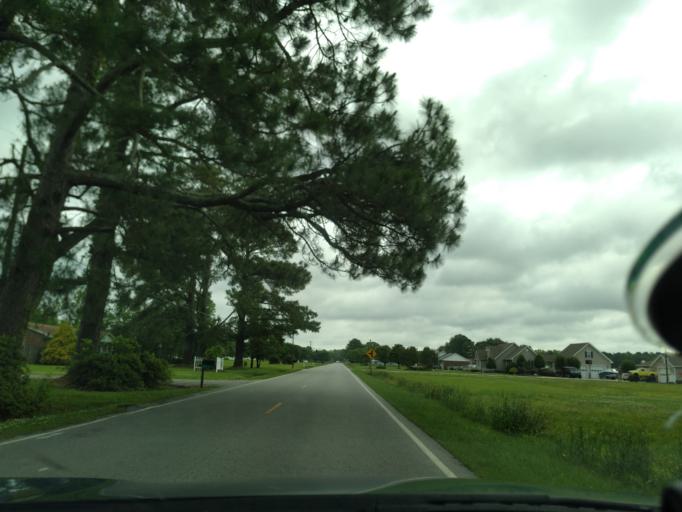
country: US
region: North Carolina
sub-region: Washington County
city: Plymouth
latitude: 35.8665
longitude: -76.7032
